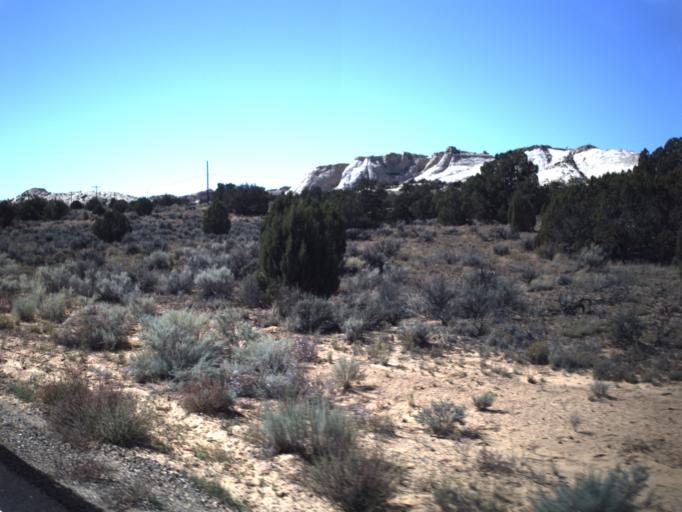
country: US
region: Utah
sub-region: Wayne County
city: Loa
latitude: 37.7637
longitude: -111.4296
